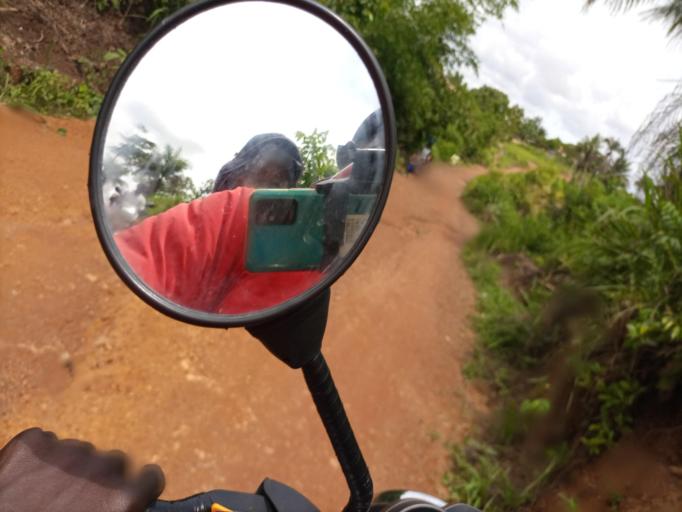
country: SL
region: Southern Province
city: Baoma
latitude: 7.9779
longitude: -11.7125
